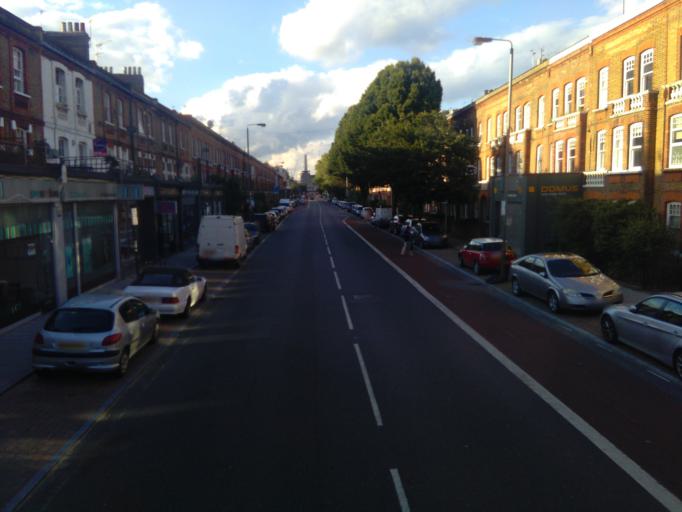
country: GB
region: England
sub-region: Greater London
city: Battersea
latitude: 51.4680
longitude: -0.1504
